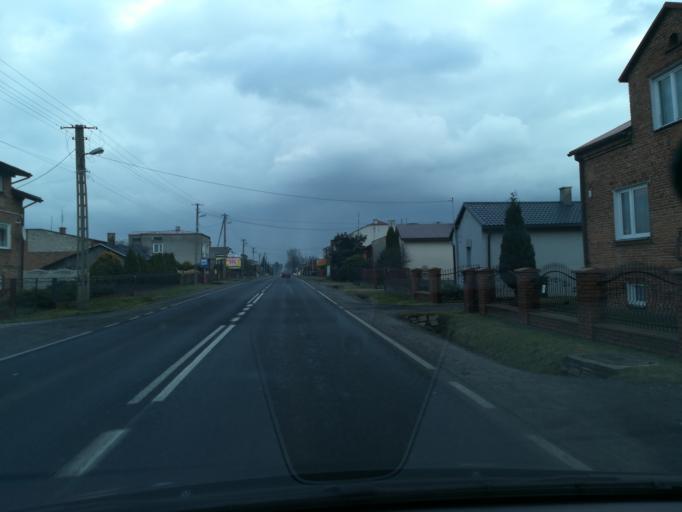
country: PL
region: Lodz Voivodeship
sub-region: Powiat radomszczanski
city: Radomsko
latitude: 51.0769
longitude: 19.3990
